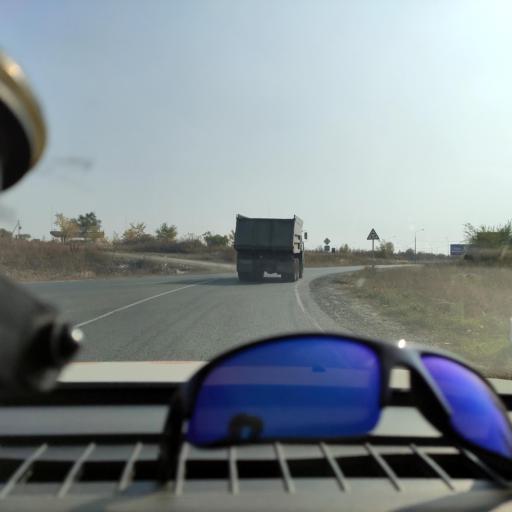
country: RU
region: Samara
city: Chapayevsk
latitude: 52.9994
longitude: 49.7675
